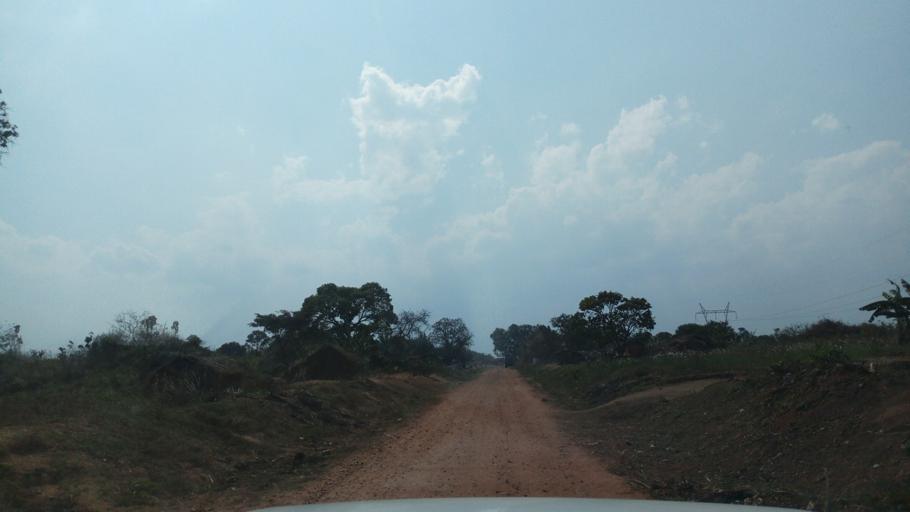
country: CD
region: Katanga
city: Kalemie
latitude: -5.5567
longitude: 29.0081
